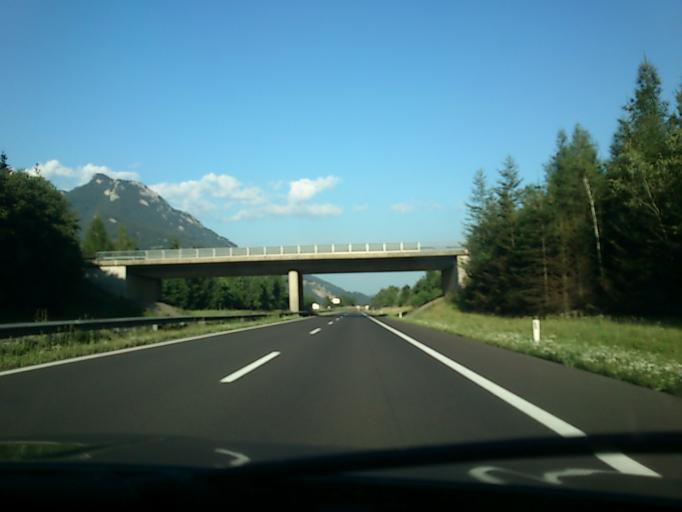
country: AT
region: Styria
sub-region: Politischer Bezirk Leoben
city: Mautern in Steiermark
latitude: 47.3965
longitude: 14.8135
